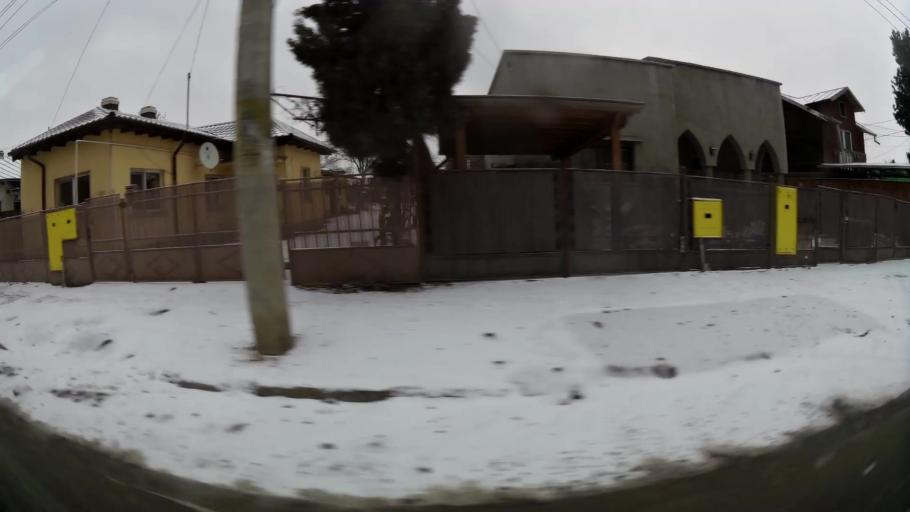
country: RO
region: Prahova
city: Ploiesti
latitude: 44.9305
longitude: 26.0393
